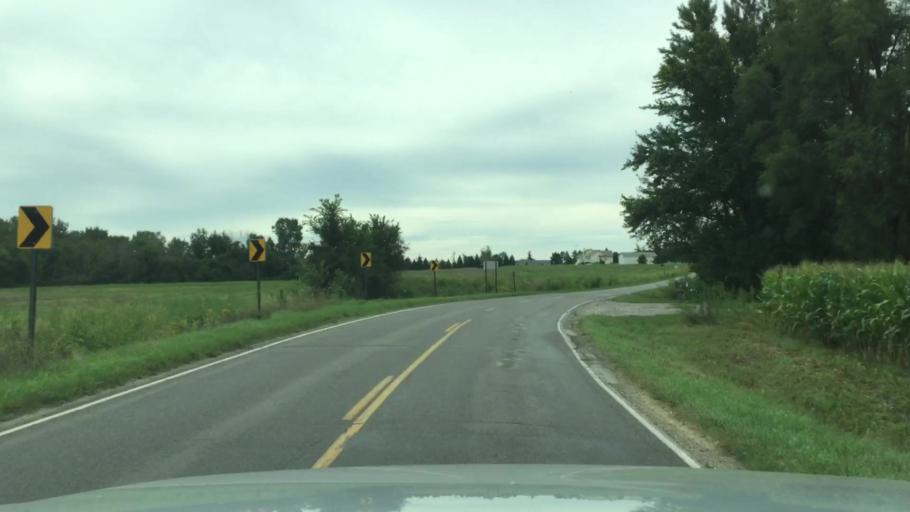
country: US
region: Michigan
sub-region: Shiawassee County
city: Durand
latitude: 42.9564
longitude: -83.9872
